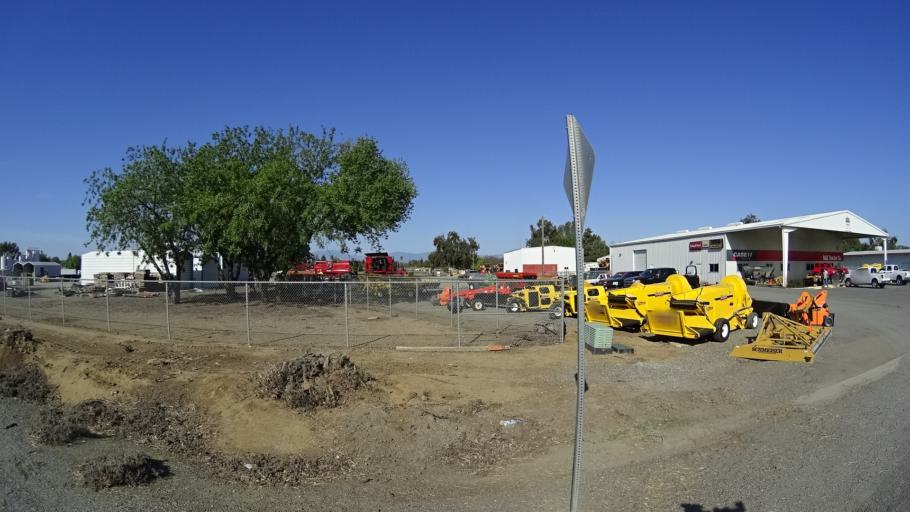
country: US
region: California
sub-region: Glenn County
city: Willows
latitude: 39.5304
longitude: -122.1934
